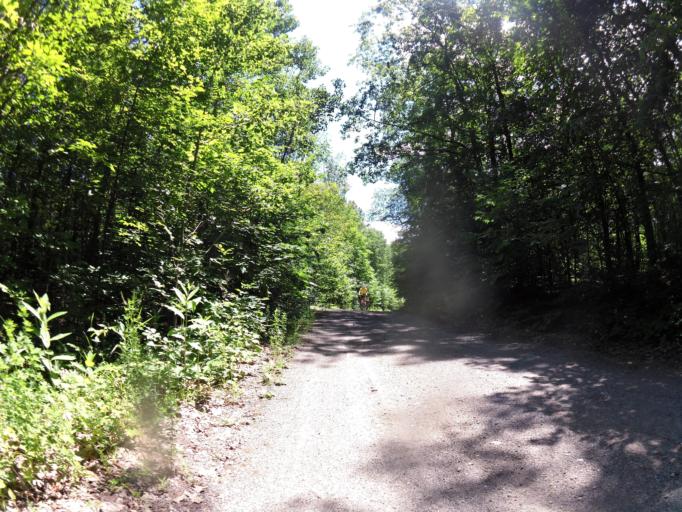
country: CA
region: Ontario
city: Perth
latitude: 45.0183
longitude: -76.6131
